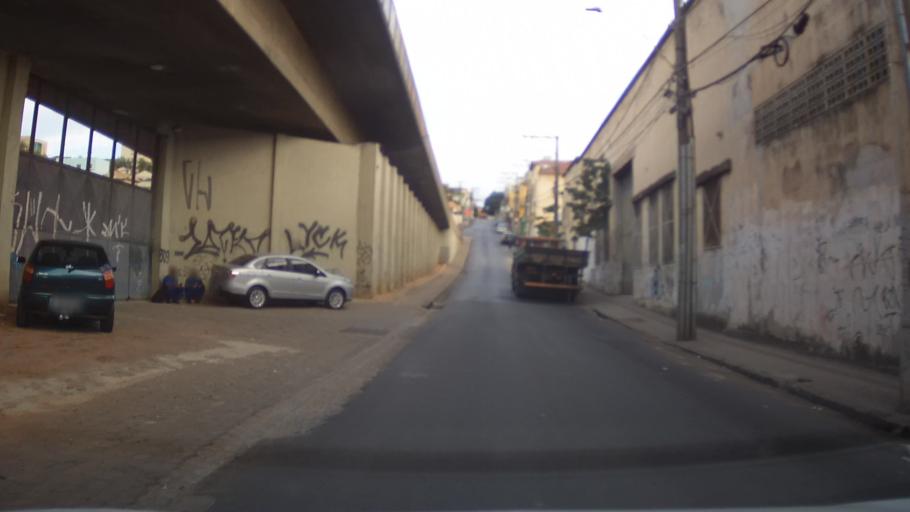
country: BR
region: Minas Gerais
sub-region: Belo Horizonte
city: Belo Horizonte
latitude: -19.9169
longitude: -43.9646
